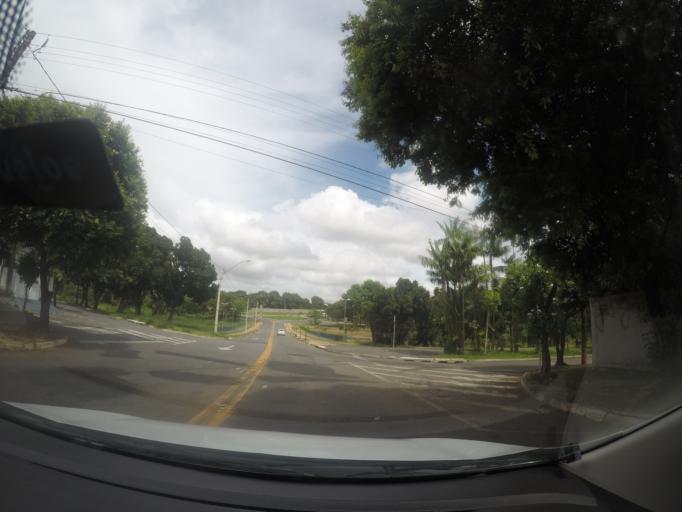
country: BR
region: Goias
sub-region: Goiania
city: Goiania
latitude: -16.7160
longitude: -49.3205
